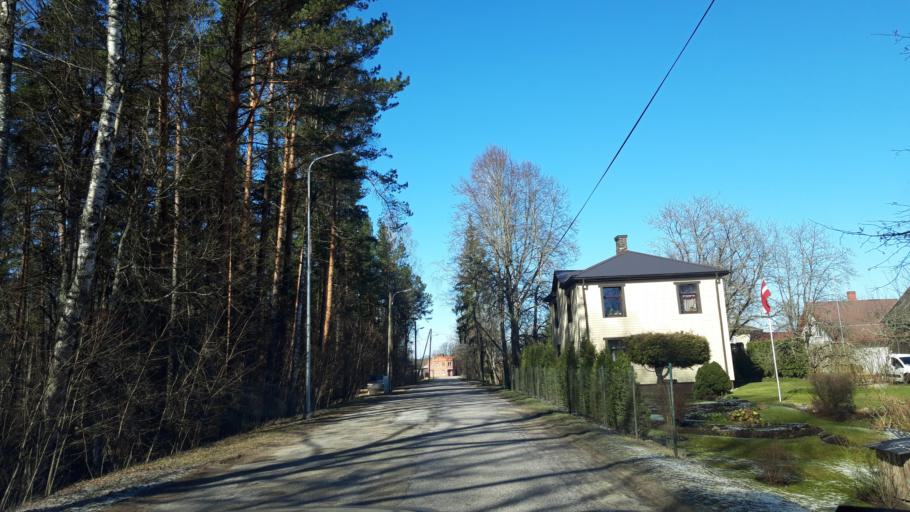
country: LV
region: Strenci
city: Strenci
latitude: 57.6221
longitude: 25.6972
